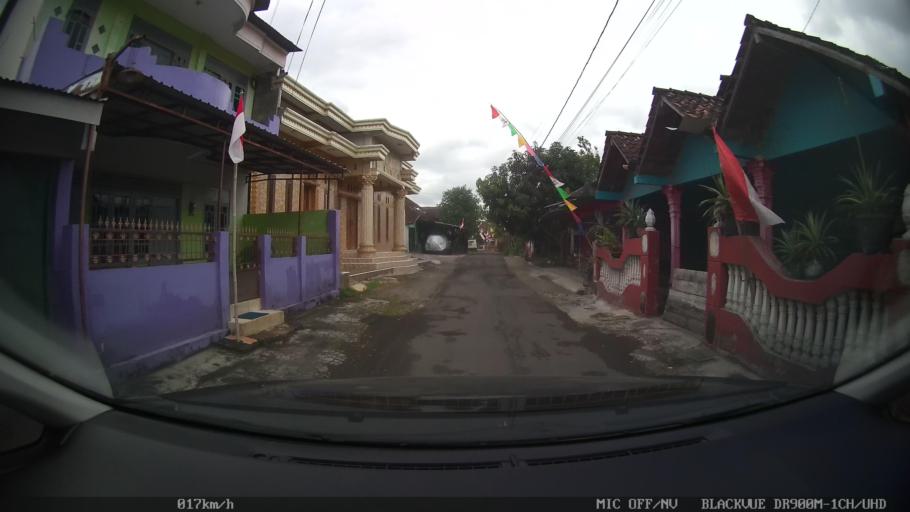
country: ID
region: Daerah Istimewa Yogyakarta
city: Sewon
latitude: -7.8328
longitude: 110.4076
